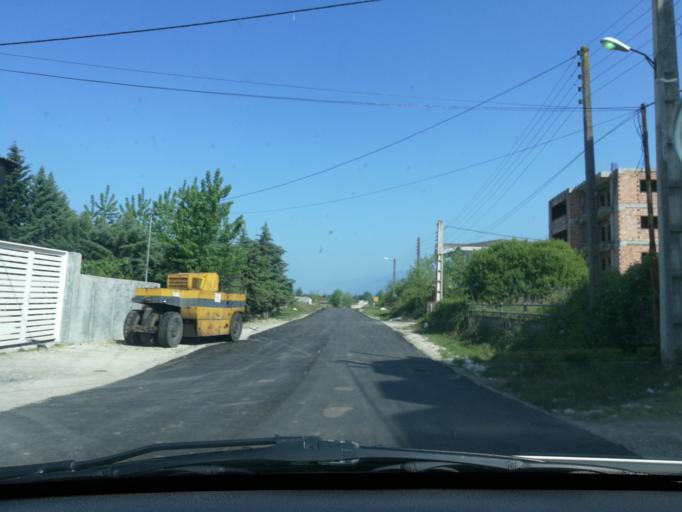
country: IR
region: Mazandaran
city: Chalus
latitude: 36.6723
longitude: 51.4322
